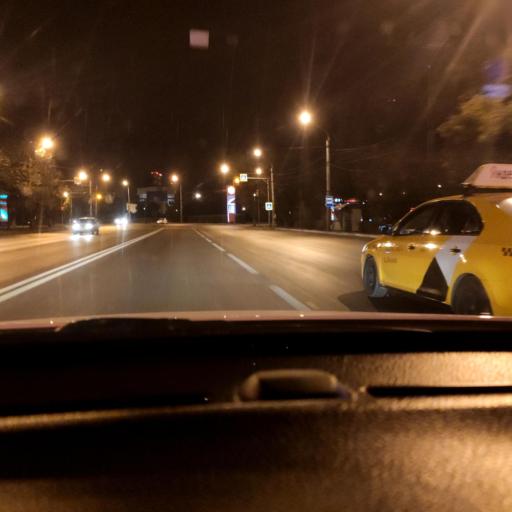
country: RU
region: Voronezj
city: Voronezh
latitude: 51.6298
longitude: 39.2306
